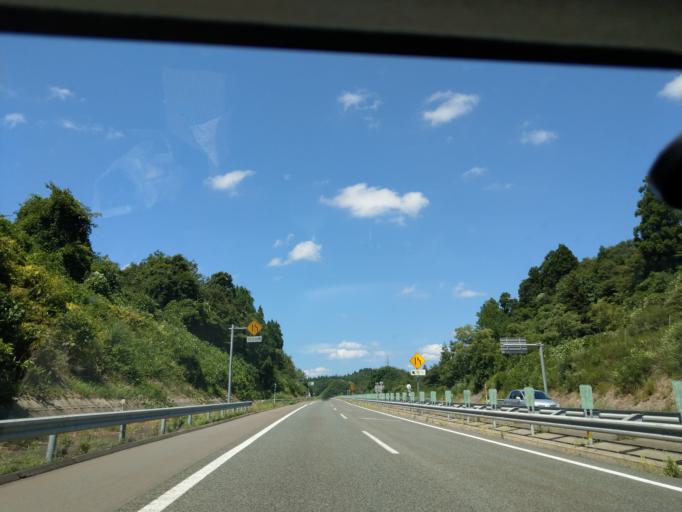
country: JP
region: Akita
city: Akita
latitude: 39.6652
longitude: 140.1885
